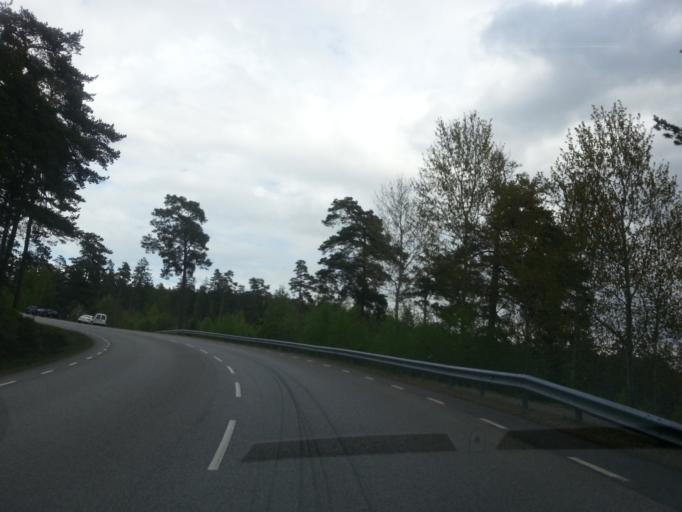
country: SE
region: OEstergoetland
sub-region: Norrkopings Kommun
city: Krokek
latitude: 58.6696
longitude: 16.3261
